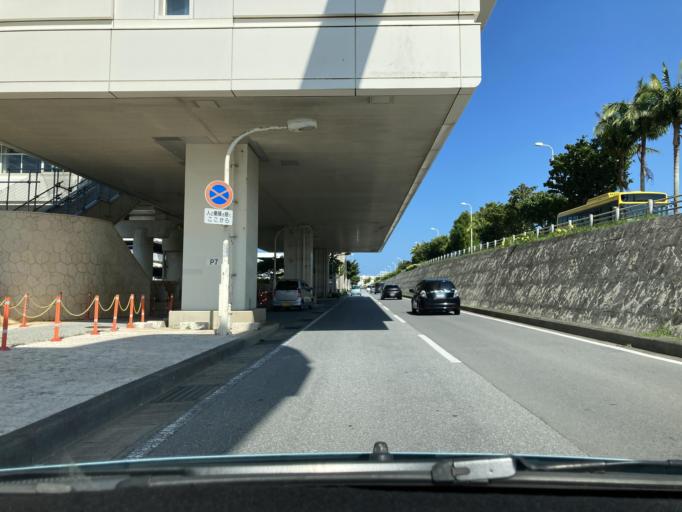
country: JP
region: Okinawa
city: Naha-shi
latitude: 26.2061
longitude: 127.6523
